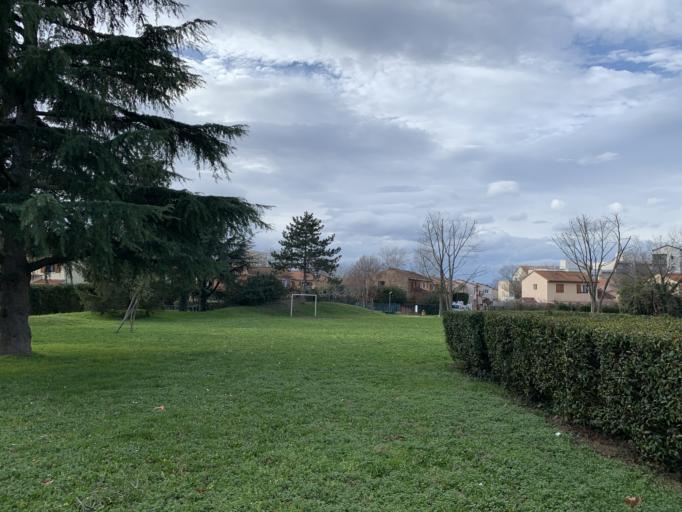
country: FR
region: Rhone-Alpes
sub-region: Departement du Rhone
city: Saint-Priest
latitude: 45.7025
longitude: 4.9348
